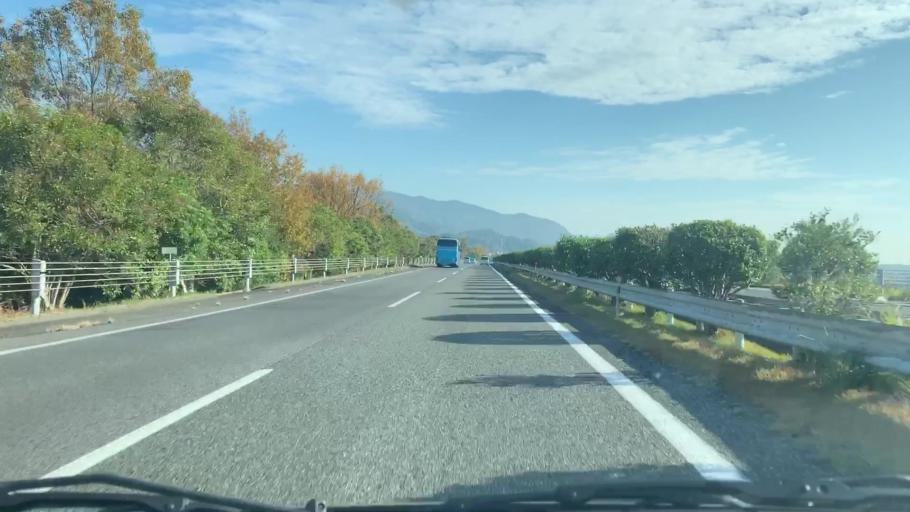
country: JP
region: Saga Prefecture
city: Saga-shi
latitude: 33.3126
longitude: 130.2525
